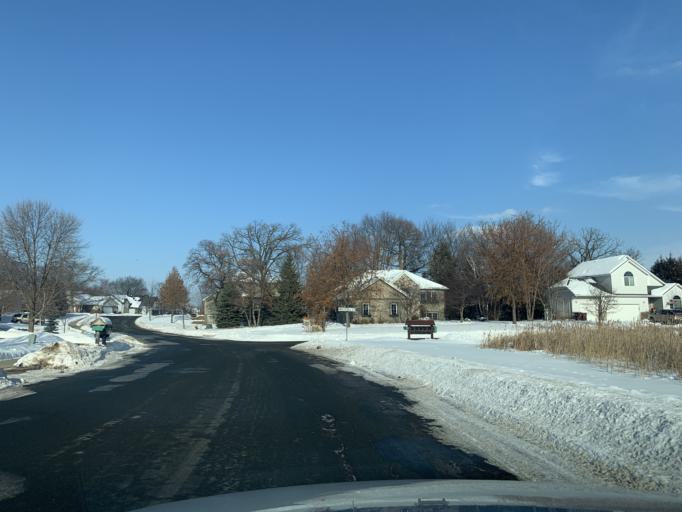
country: US
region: Minnesota
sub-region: Wright County
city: Buffalo
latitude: 45.2027
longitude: -93.8337
